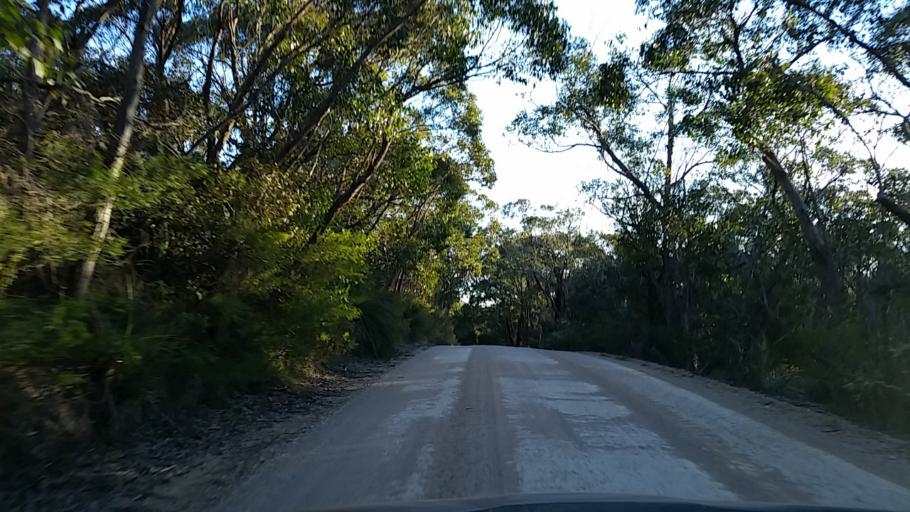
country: AU
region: South Australia
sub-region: Alexandrina
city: Mount Compass
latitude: -35.3026
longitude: 138.6786
